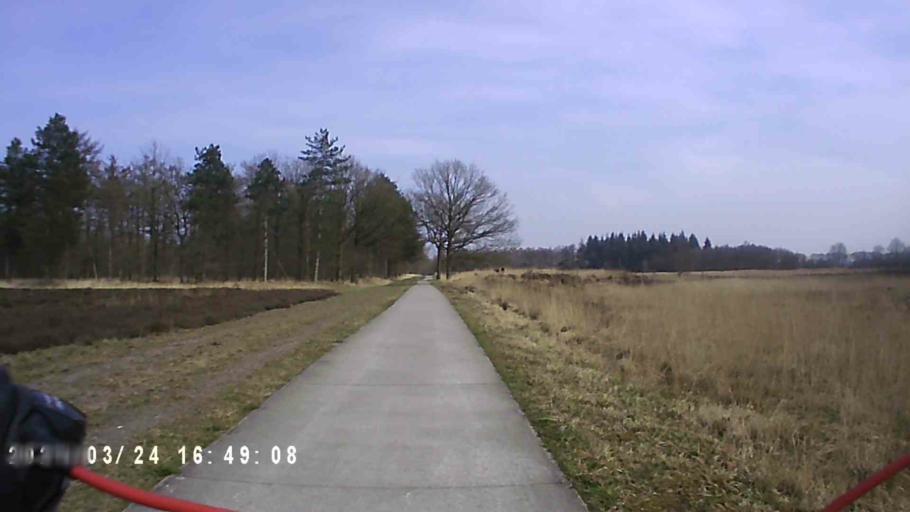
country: NL
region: Groningen
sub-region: Gemeente Leek
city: Leek
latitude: 53.0483
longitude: 6.2886
